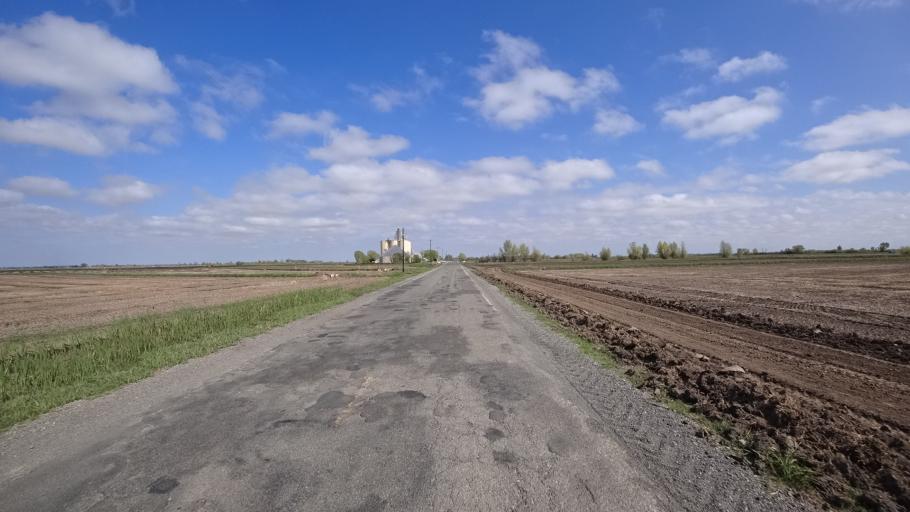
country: US
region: California
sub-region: Colusa County
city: Colusa
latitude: 39.3794
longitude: -121.9362
